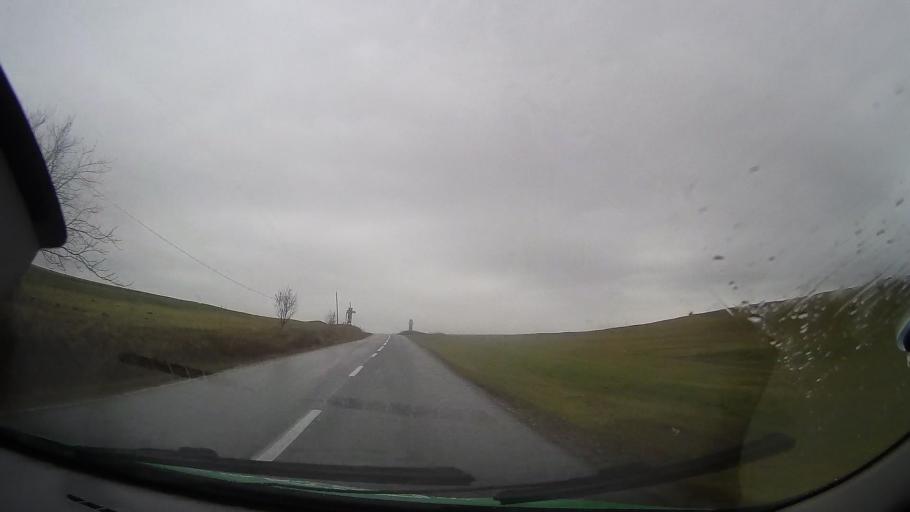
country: RO
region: Bistrita-Nasaud
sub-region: Comuna Monor
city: Monor
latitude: 46.9591
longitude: 24.6723
